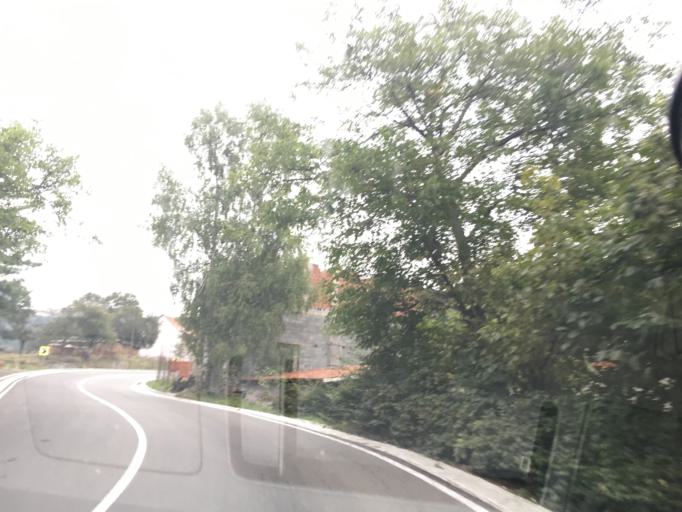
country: RS
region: Central Serbia
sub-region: Moravicki Okrug
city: Gornji Milanovac
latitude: 44.1433
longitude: 20.4972
